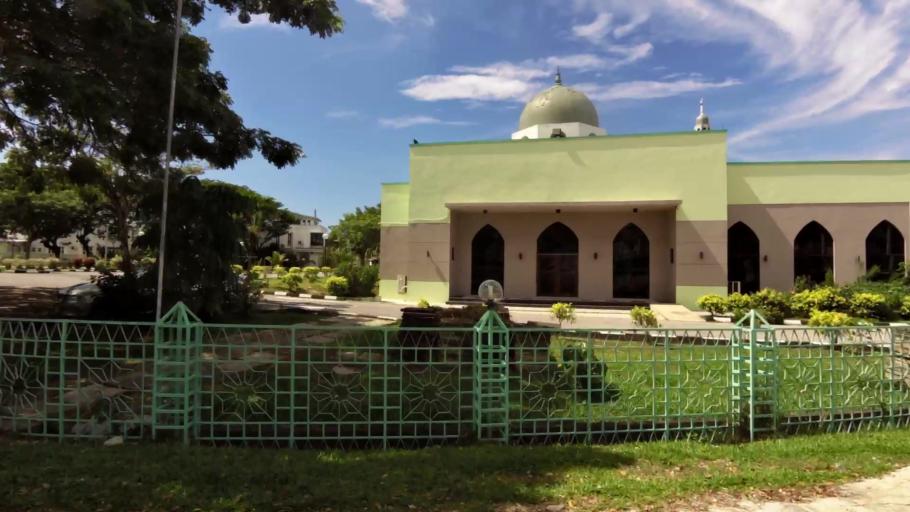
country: BN
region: Brunei and Muara
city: Bandar Seri Begawan
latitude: 4.9682
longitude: 114.9445
